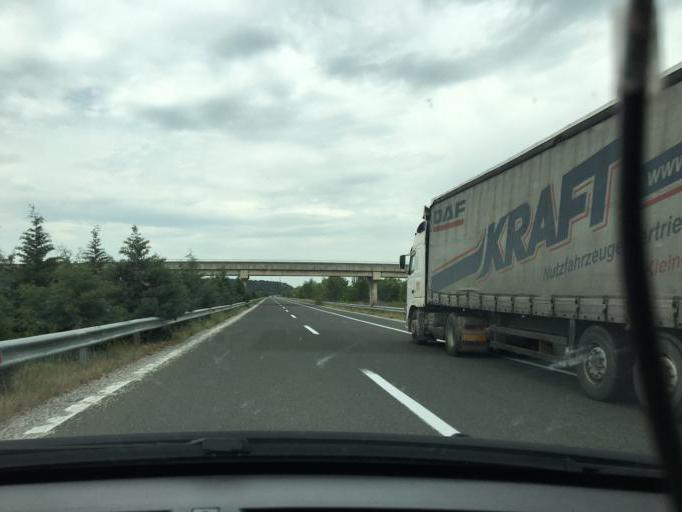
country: MK
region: Negotino
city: Negotino
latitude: 41.5242
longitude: 22.0667
